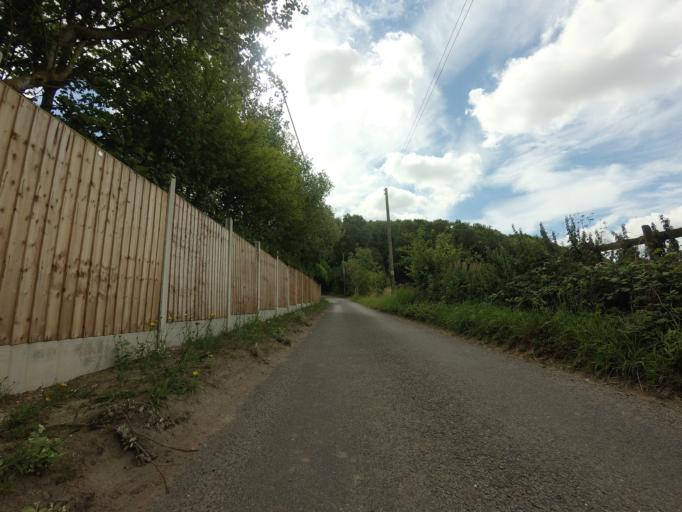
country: GB
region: England
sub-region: Kent
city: Swanley
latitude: 51.3693
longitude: 0.1442
